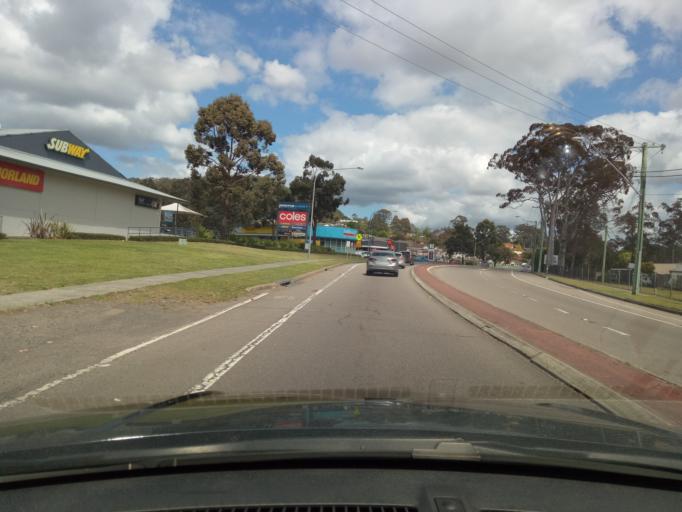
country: AU
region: New South Wales
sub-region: Gosford Shire
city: Lisarow
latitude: -33.3844
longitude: 151.3675
